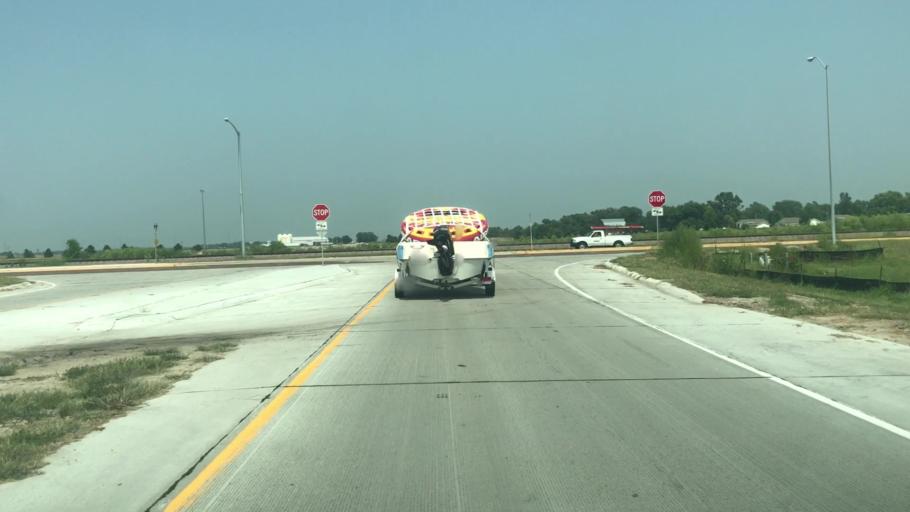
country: US
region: Nebraska
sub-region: Hall County
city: Grand Island
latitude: 40.9526
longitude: -98.3826
